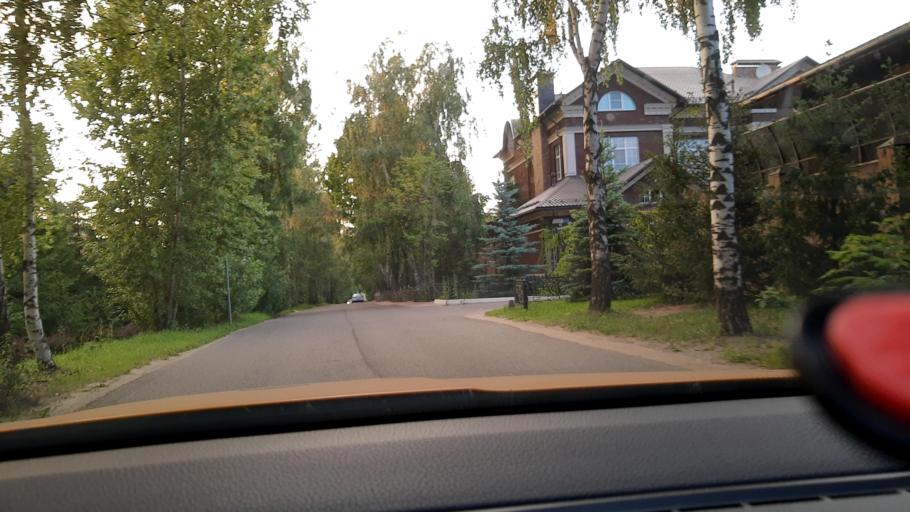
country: RU
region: Moskovskaya
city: Barvikha
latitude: 55.7298
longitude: 37.2899
